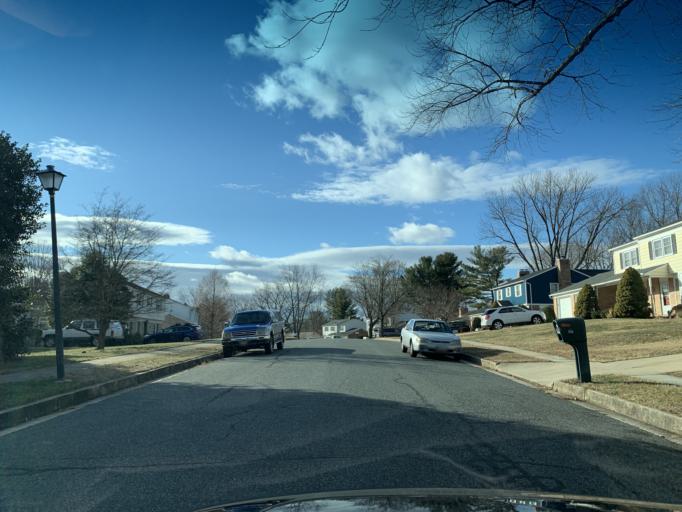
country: US
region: Maryland
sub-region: Harford County
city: South Bel Air
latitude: 39.5332
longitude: -76.3277
